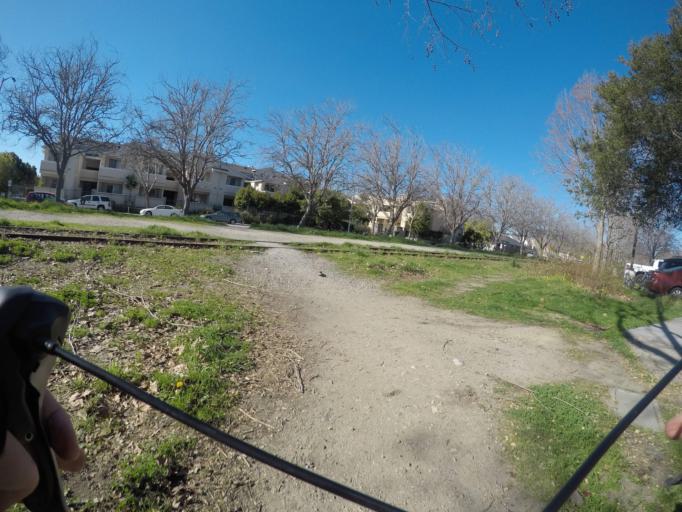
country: US
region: California
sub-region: Santa Cruz County
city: Santa Cruz
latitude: 36.9658
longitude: -122.0280
